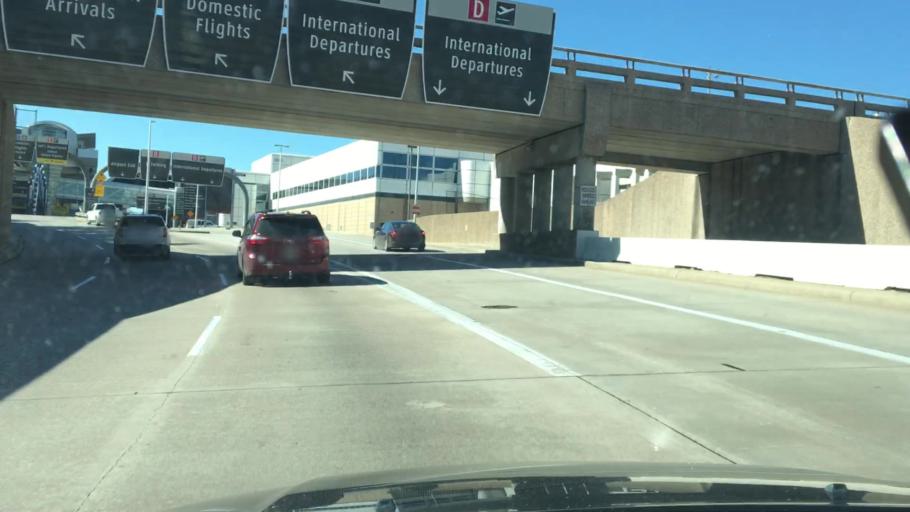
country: US
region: Texas
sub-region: Harris County
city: Humble
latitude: 29.9873
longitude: -95.3307
